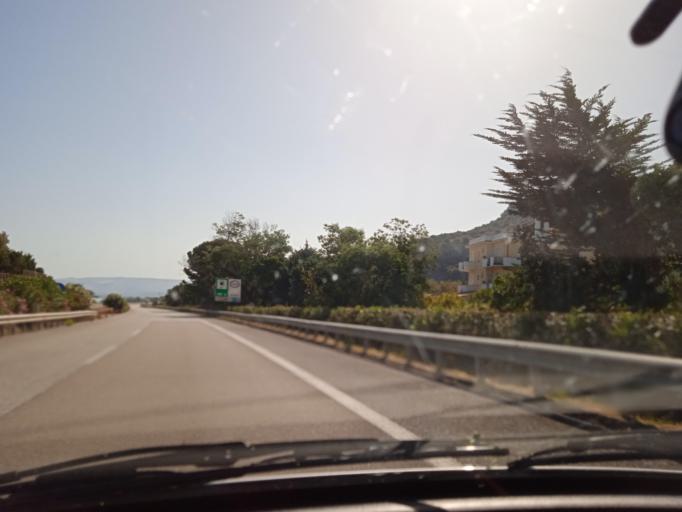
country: IT
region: Sicily
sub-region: Messina
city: Acquedolci
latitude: 38.0493
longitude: 14.5837
